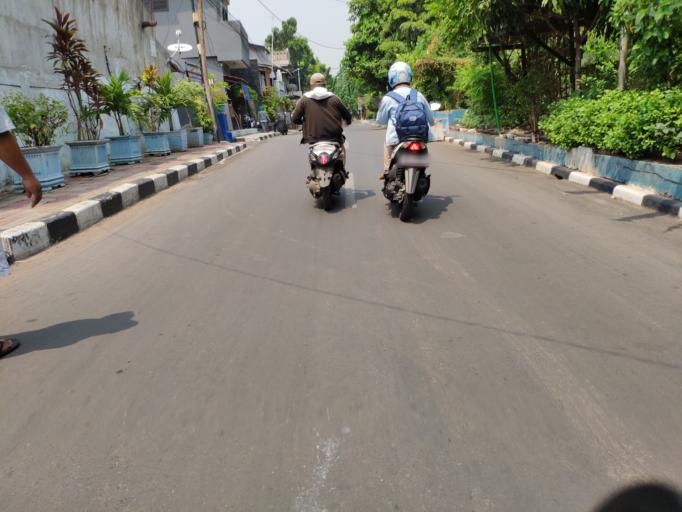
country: ID
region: Jakarta Raya
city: Jakarta
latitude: -6.2015
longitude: 106.8689
